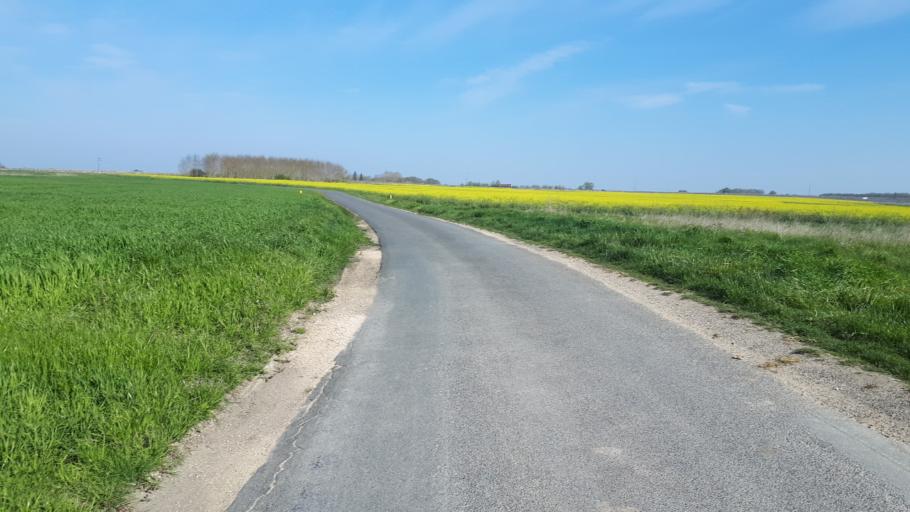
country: FR
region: Centre
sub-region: Departement du Loir-et-Cher
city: Contres
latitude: 47.3836
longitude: 1.3898
